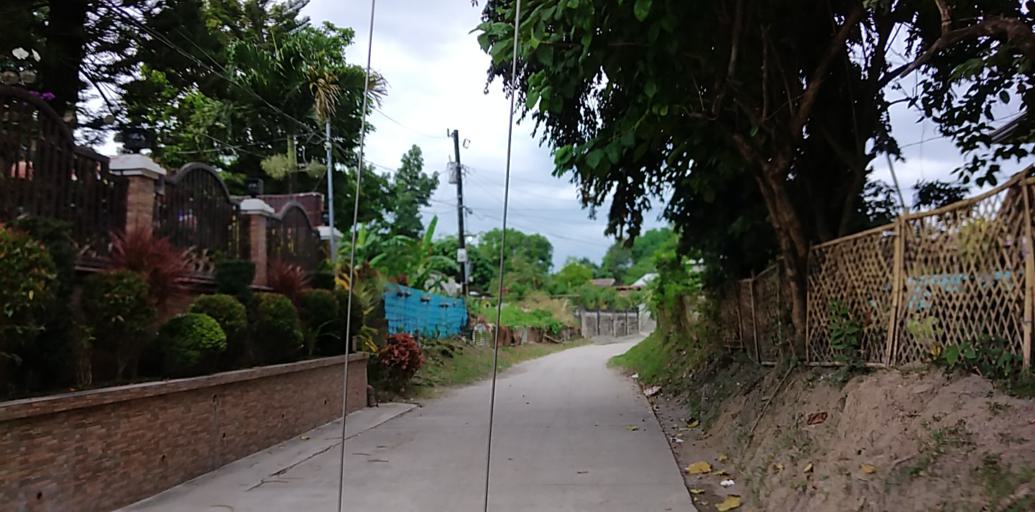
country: PH
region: Central Luzon
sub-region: Province of Pampanga
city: Pulung Santol
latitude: 15.0421
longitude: 120.5639
